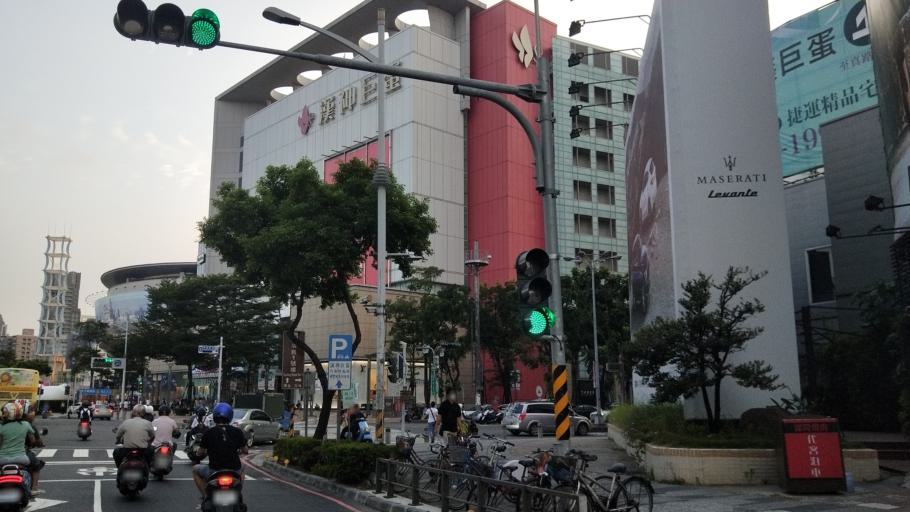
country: TW
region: Kaohsiung
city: Kaohsiung
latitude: 22.6709
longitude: 120.3036
